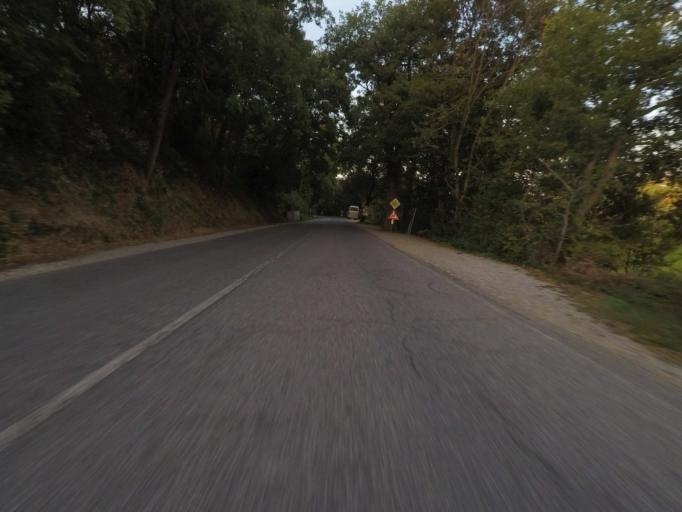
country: IT
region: Tuscany
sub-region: Provincia di Siena
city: Torrita di Siena
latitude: 43.1346
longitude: 11.7298
